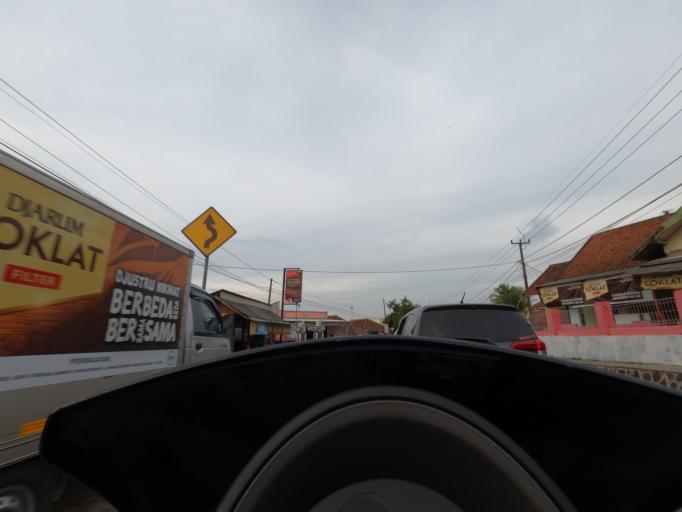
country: ID
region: West Java
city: Lembang
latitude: -6.6607
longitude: 107.7111
